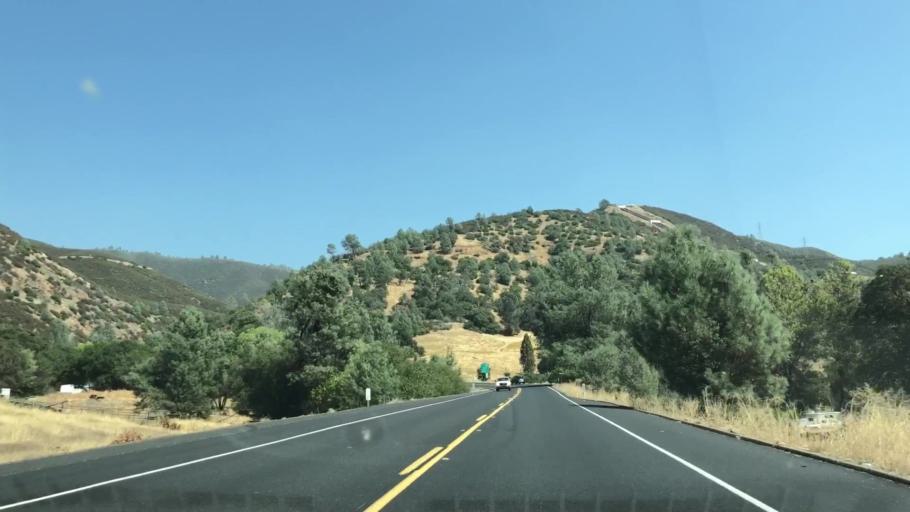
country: US
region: California
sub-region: Tuolumne County
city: Tuolumne City
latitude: 37.8138
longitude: -120.3020
